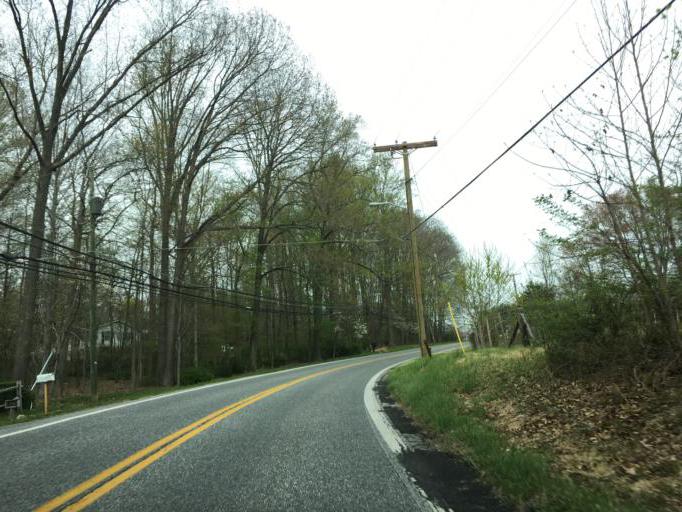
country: US
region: Maryland
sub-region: Baltimore County
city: Hunt Valley
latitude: 39.5027
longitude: -76.5772
